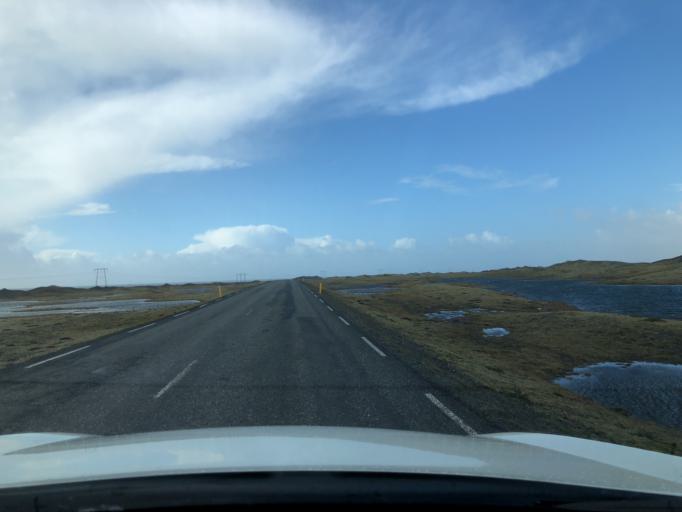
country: IS
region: East
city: Hoefn
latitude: 64.0823
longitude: -16.1072
